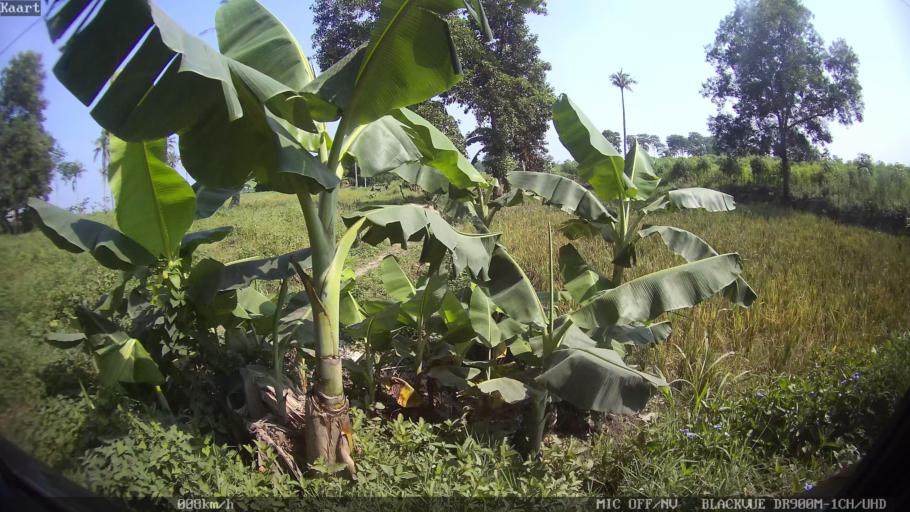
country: ID
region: Lampung
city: Natar
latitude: -5.2645
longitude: 105.2076
